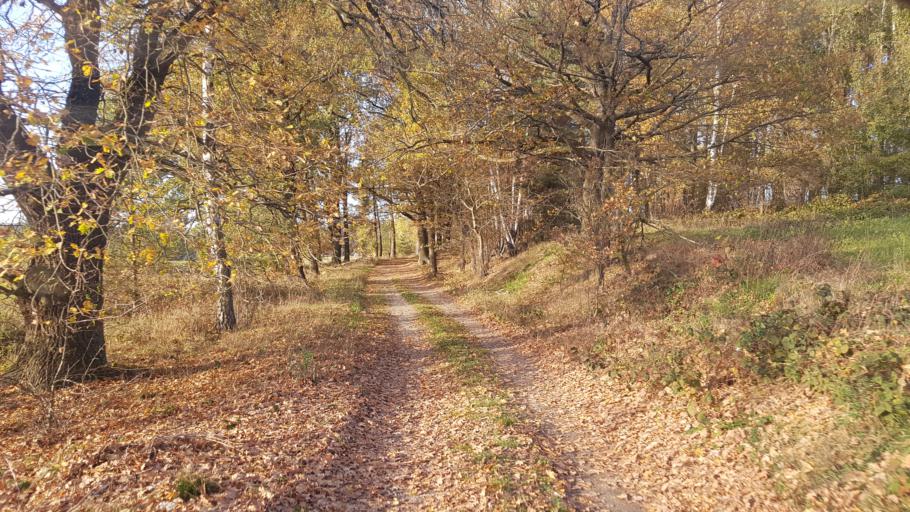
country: DE
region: Brandenburg
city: Calau
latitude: 51.6972
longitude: 13.9584
